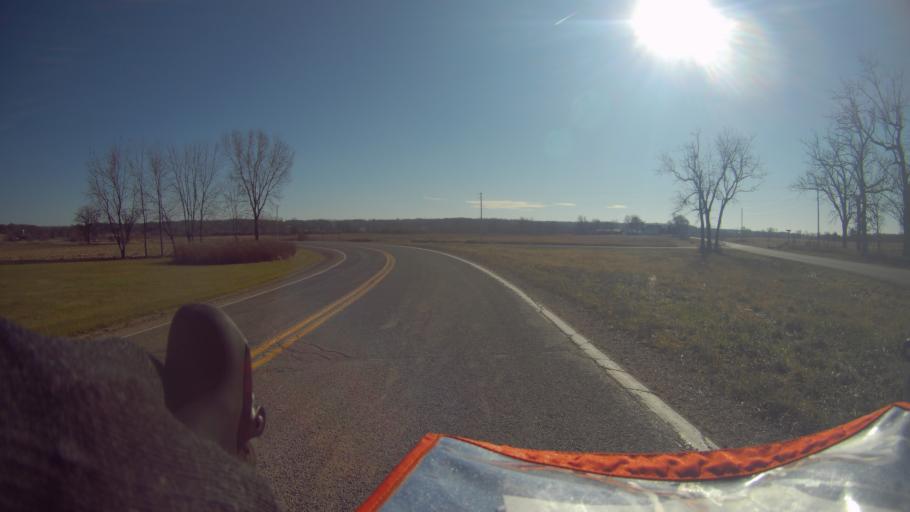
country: US
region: Wisconsin
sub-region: Dane County
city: Fitchburg
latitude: 42.8932
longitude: -89.4480
